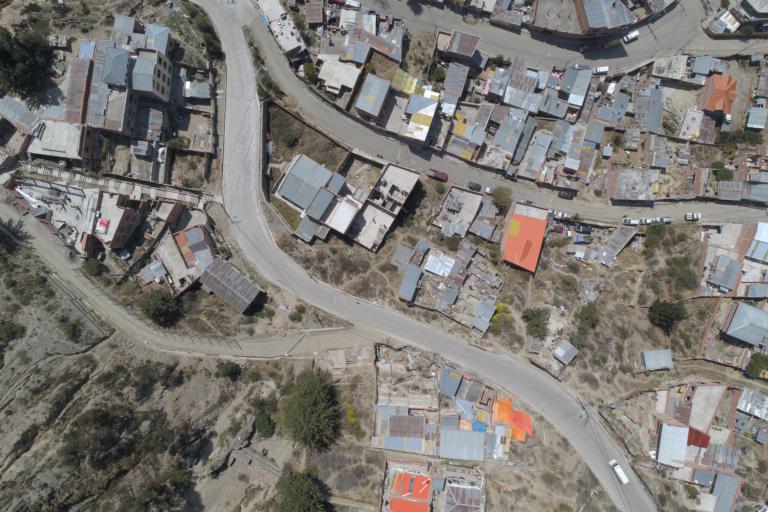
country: BO
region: La Paz
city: La Paz
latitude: -16.4980
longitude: -68.0987
